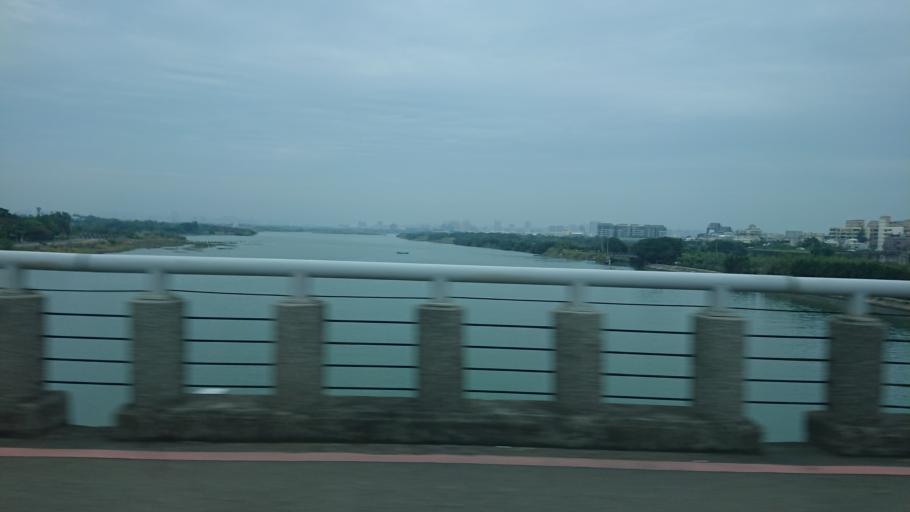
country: TW
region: Taiwan
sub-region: Hsinchu
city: Hsinchu
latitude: 24.8429
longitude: 120.9413
